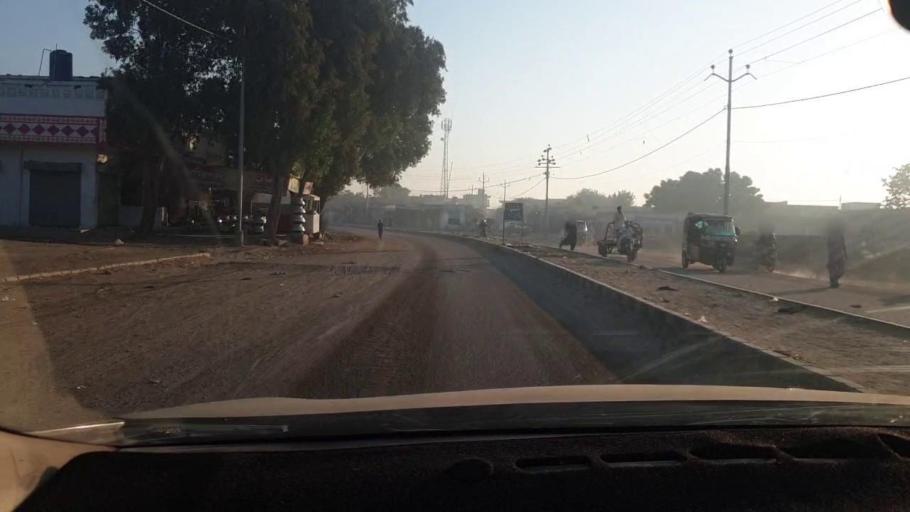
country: PK
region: Sindh
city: Malir Cantonment
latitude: 25.0110
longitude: 67.1662
